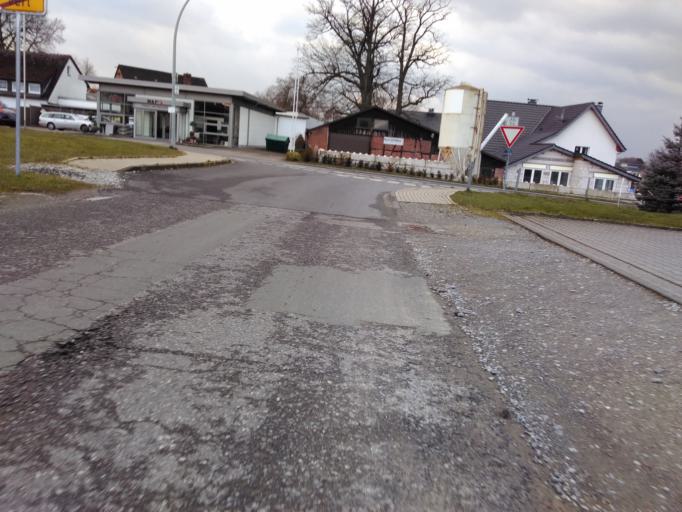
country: DE
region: North Rhine-Westphalia
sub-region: Regierungsbezirk Detmold
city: Verl
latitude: 51.8792
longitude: 8.4811
